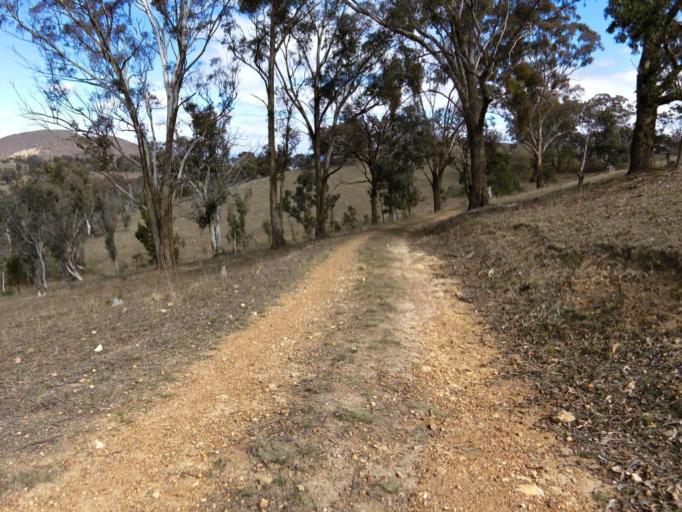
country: AU
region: Australian Capital Territory
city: Kaleen
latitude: -35.2106
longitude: 149.1888
